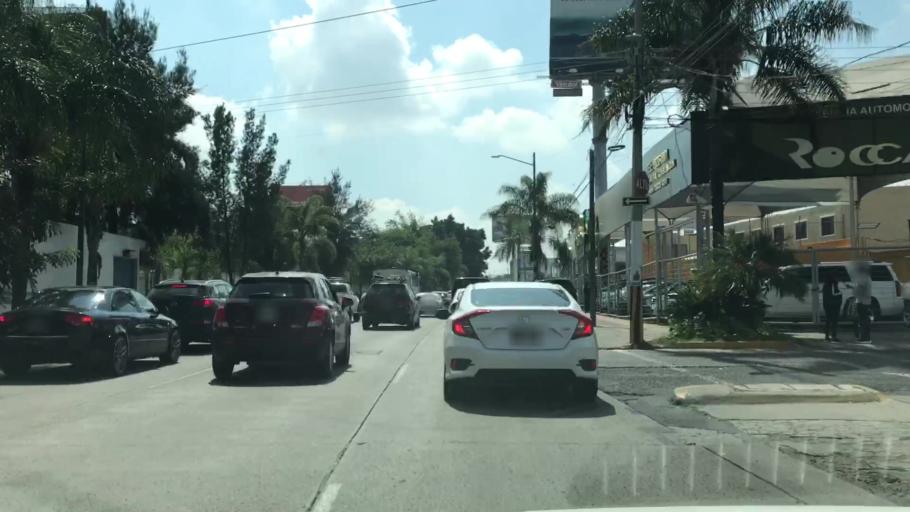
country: MX
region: Jalisco
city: Guadalajara
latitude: 20.6410
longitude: -103.4200
